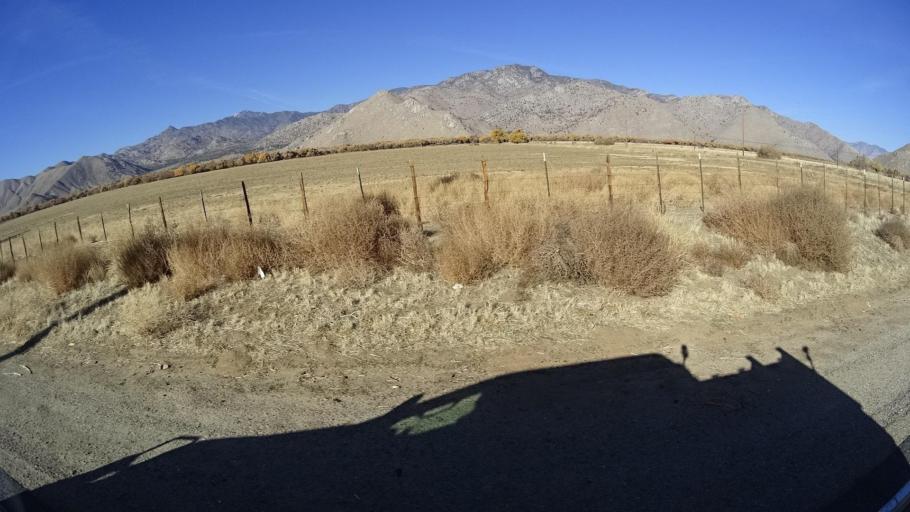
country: US
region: California
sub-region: Kern County
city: Weldon
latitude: 35.6669
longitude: -118.2729
